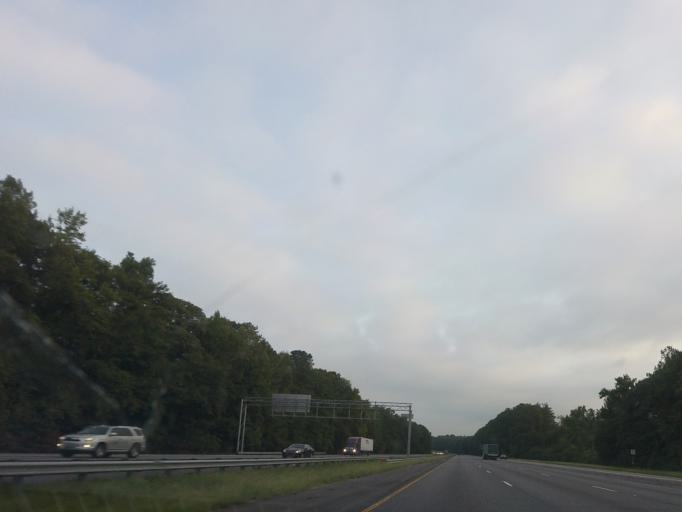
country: US
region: Georgia
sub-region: Monroe County
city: Forsyth
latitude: 33.1155
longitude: -84.0033
